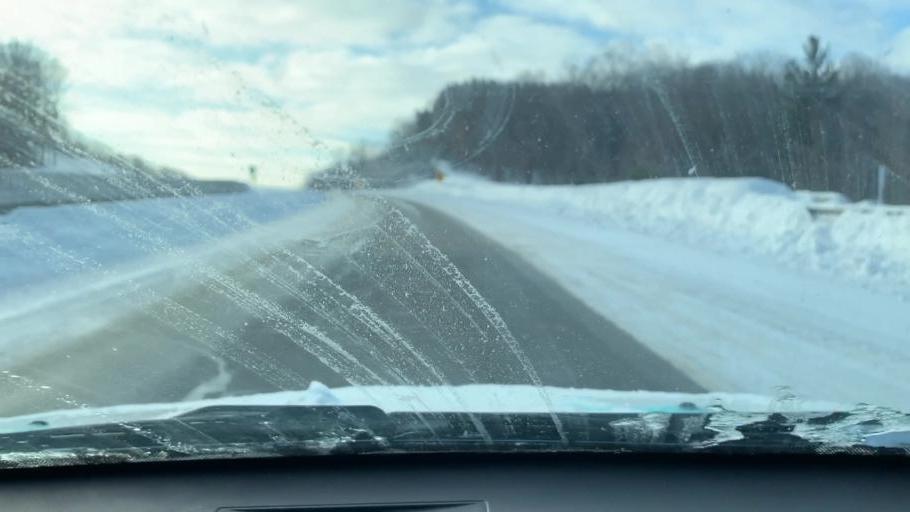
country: US
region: Michigan
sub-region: Wexford County
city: Cadillac
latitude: 44.3001
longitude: -85.3924
